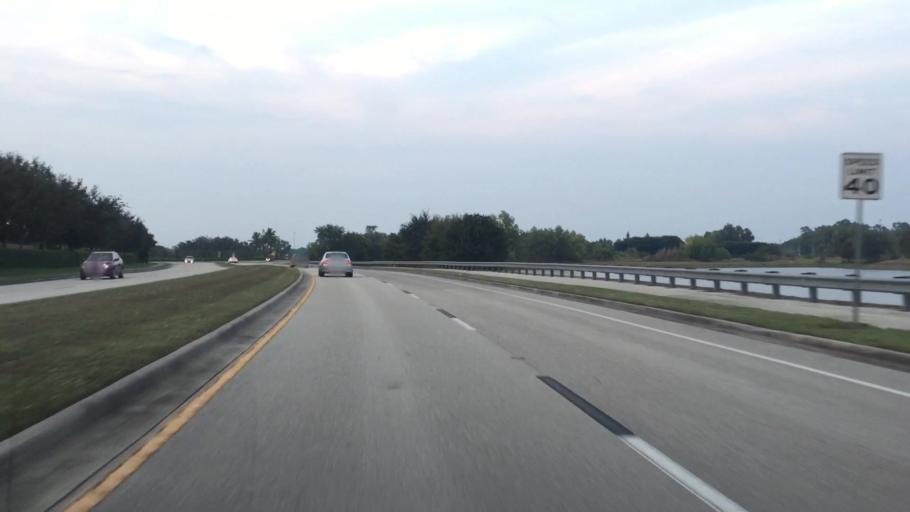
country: US
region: Florida
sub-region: Lee County
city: Estero
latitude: 26.4167
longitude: -81.8052
